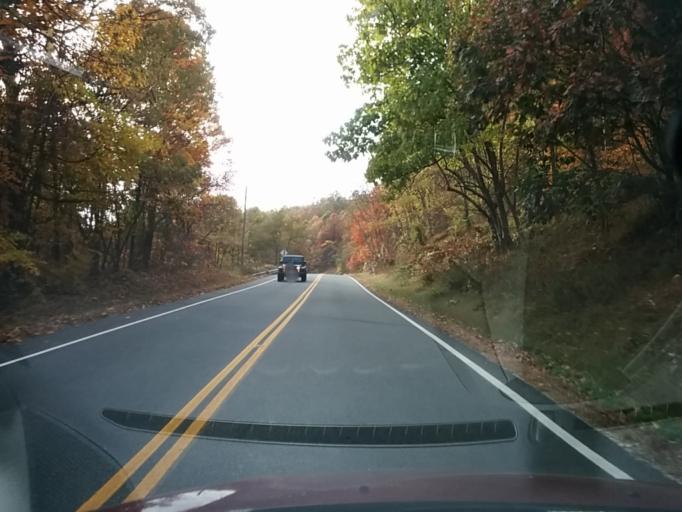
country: US
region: Virginia
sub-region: Nelson County
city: Nellysford
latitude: 37.9049
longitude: -78.9728
